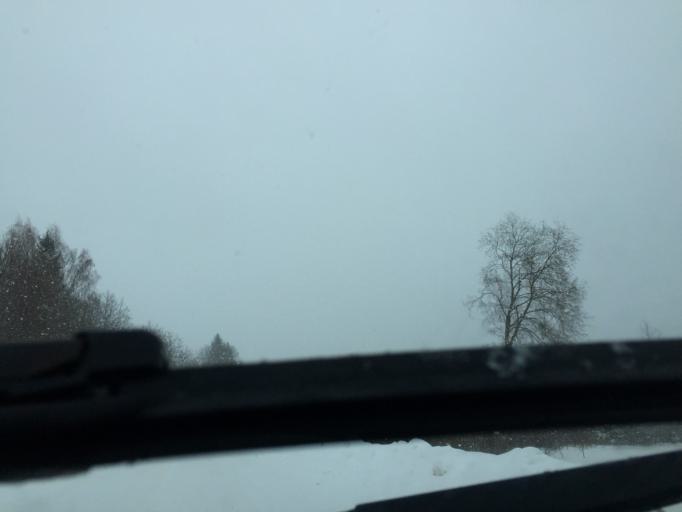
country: LV
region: Amatas Novads
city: Drabesi
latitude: 57.0859
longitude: 25.3563
